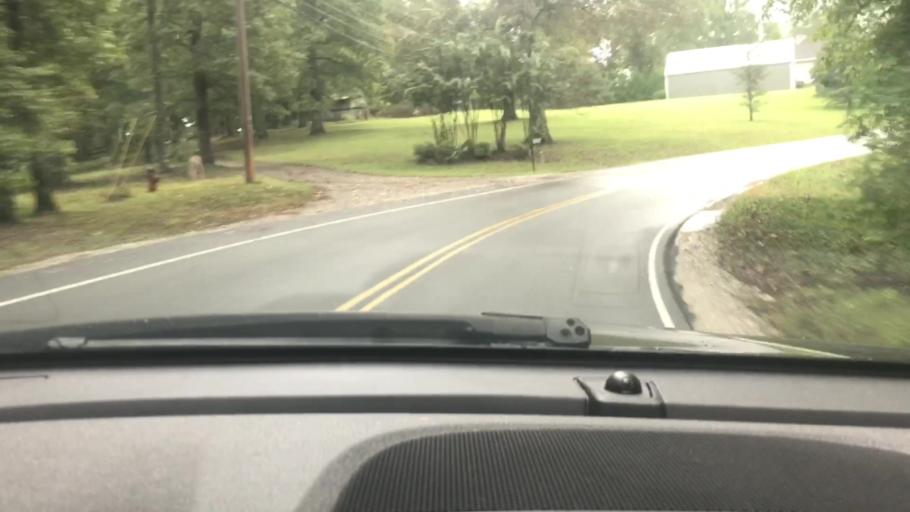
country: US
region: Tennessee
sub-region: Cheatham County
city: Kingston Springs
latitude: 36.1036
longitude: -87.1355
